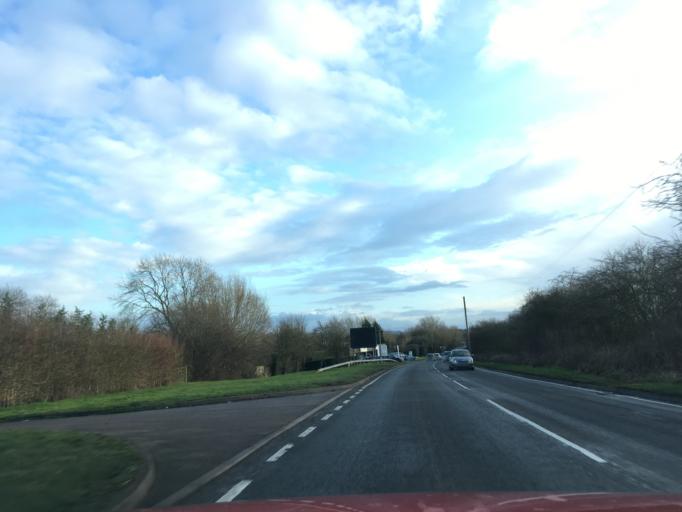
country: GB
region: England
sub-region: Warwickshire
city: Stratford-upon-Avon
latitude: 52.2165
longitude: -1.7292
